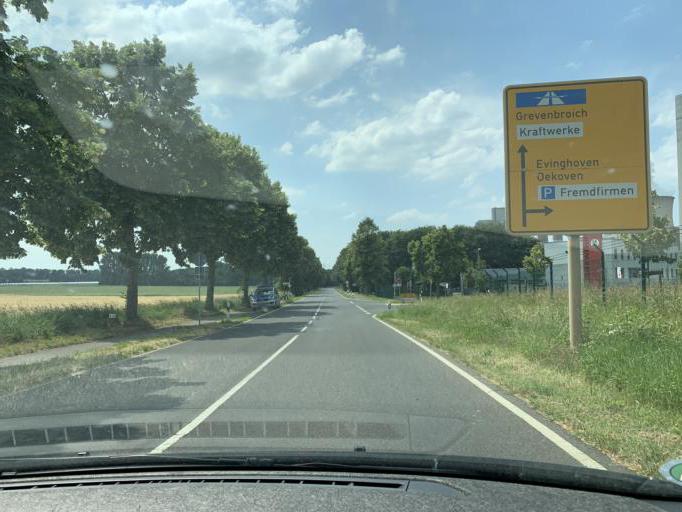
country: DE
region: North Rhine-Westphalia
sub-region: Regierungsbezirk Dusseldorf
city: Rommerskirchen
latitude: 51.0347
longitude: 6.6258
